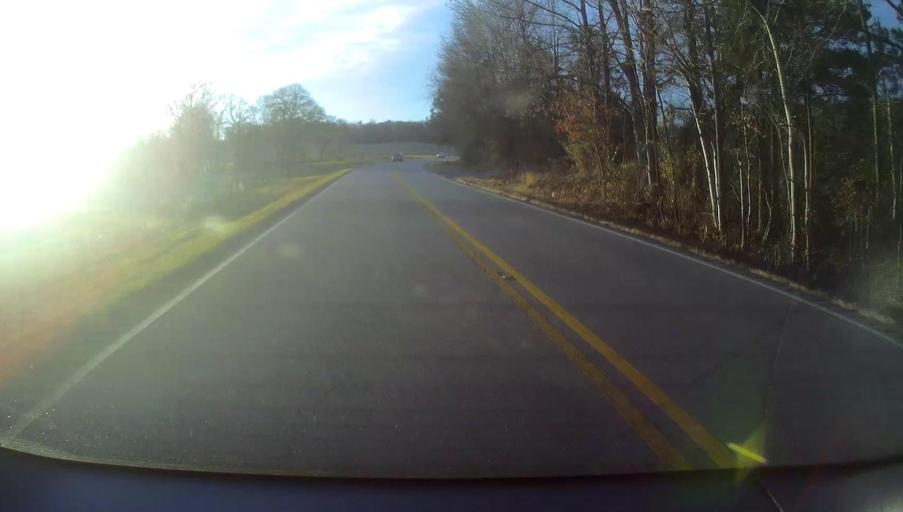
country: US
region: Alabama
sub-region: Saint Clair County
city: Steele
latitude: 34.0722
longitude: -86.3258
